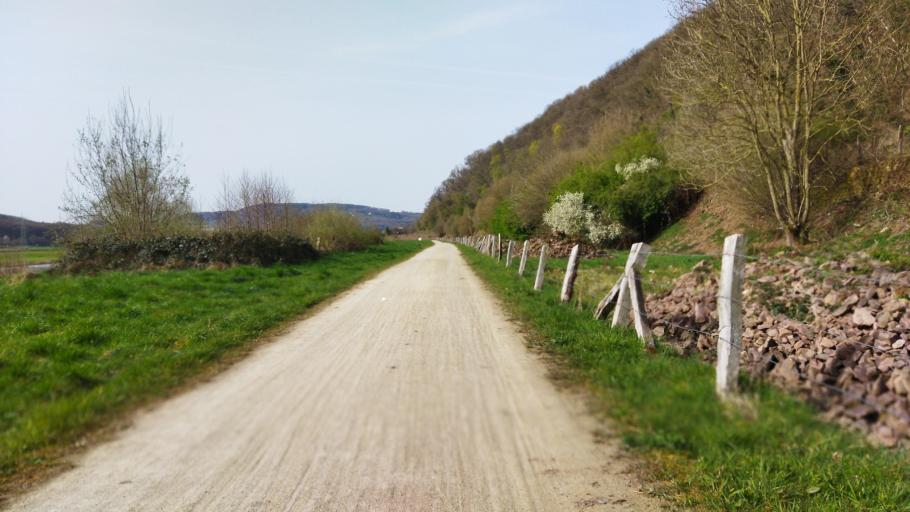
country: DE
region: North Rhine-Westphalia
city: Porta Westfalica
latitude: 52.1849
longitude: 8.9257
